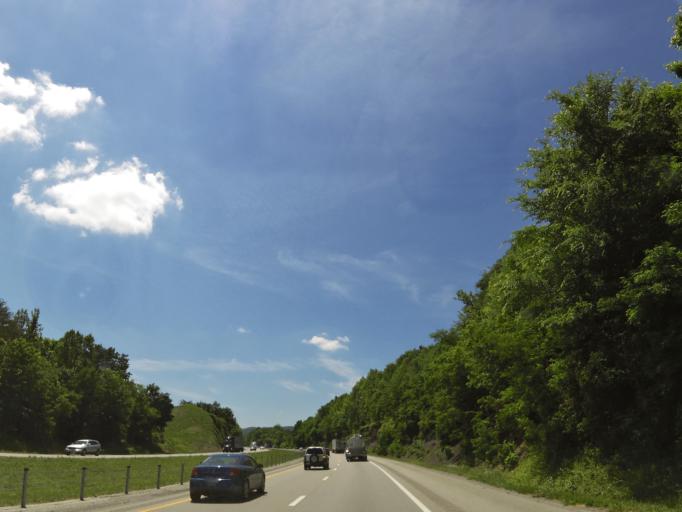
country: US
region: Kentucky
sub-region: Whitley County
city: Williamsburg
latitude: 36.7477
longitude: -84.1766
